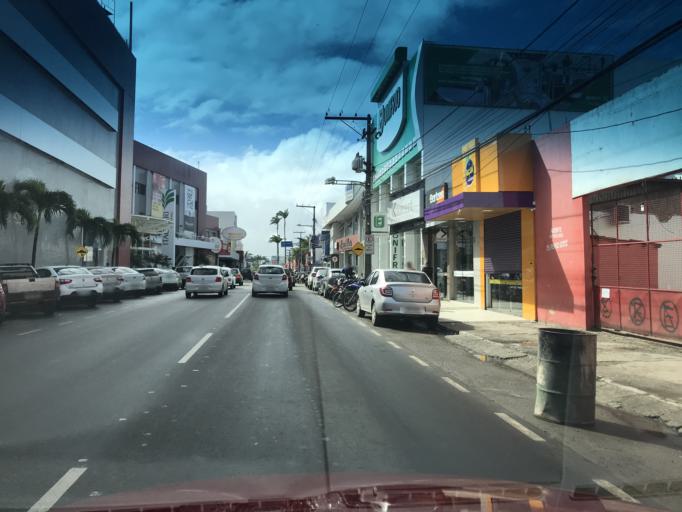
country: BR
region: Bahia
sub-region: Santo Antonio De Jesus
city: Santo Antonio de Jesus
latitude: -12.9663
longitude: -39.2684
